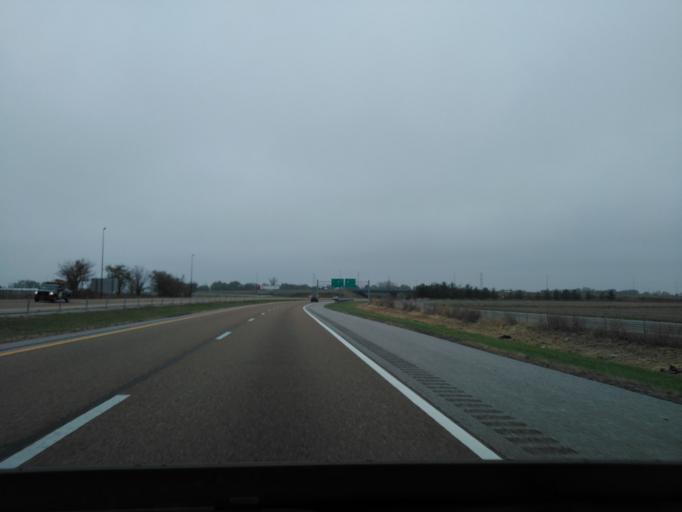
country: US
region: Illinois
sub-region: Madison County
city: Troy
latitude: 38.7226
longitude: -89.9151
